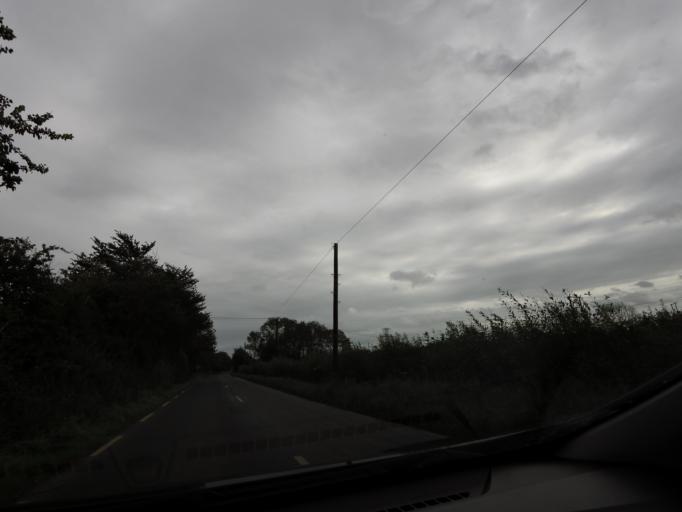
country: IE
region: Leinster
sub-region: Uibh Fhaili
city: Ferbane
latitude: 53.2274
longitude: -7.8004
